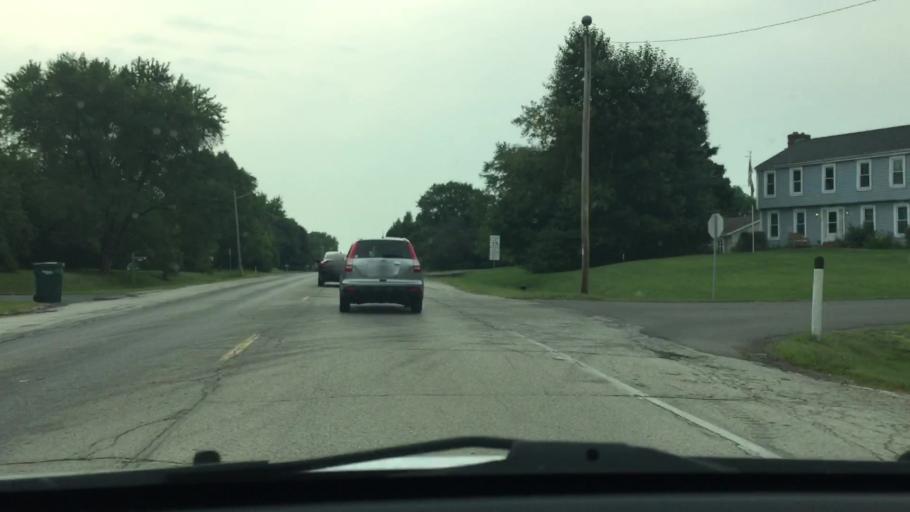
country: US
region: Wisconsin
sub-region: Waukesha County
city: New Berlin
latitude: 42.9955
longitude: -88.0970
